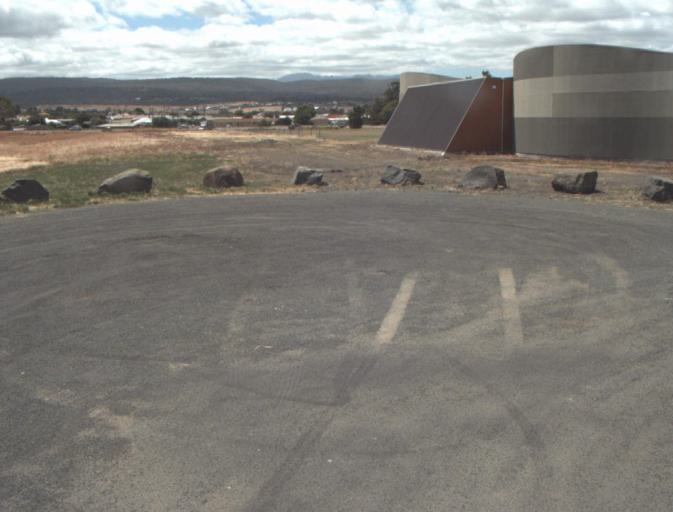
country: AU
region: Tasmania
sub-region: Launceston
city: Launceston
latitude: -41.4193
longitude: 147.1263
